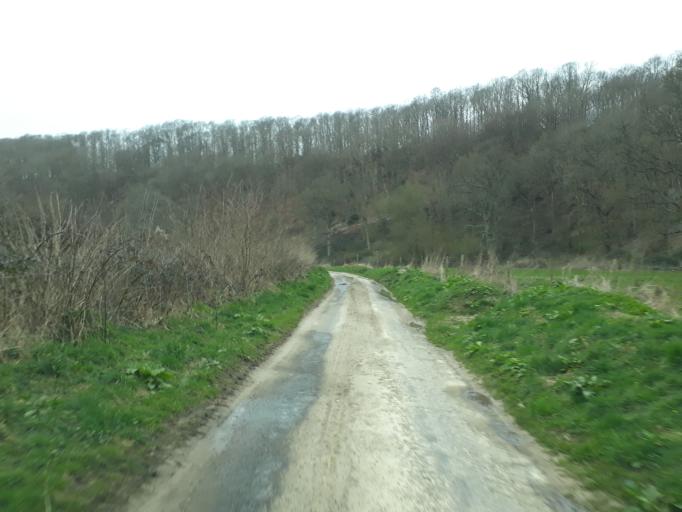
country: FR
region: Haute-Normandie
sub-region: Departement de la Seine-Maritime
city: Les Loges
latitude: 49.6688
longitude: 0.2799
